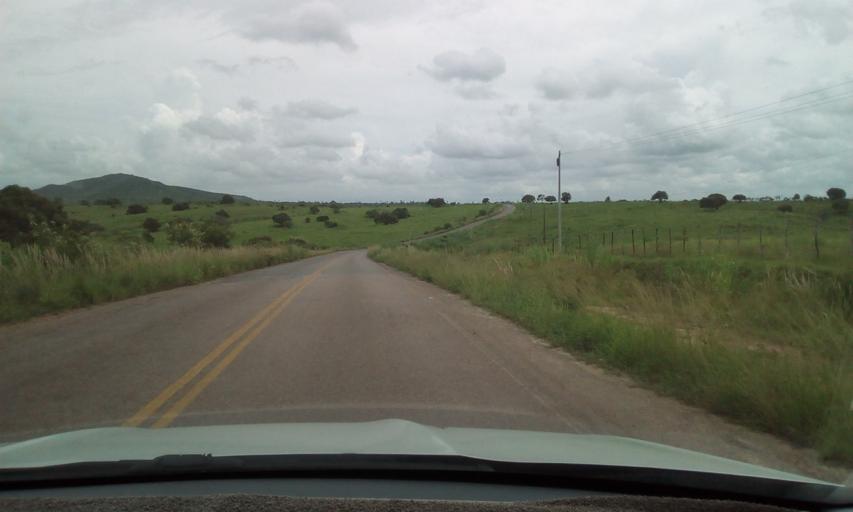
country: BR
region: Paraiba
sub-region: Gurinhem
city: Gurinhem
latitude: -7.1646
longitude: -35.3552
